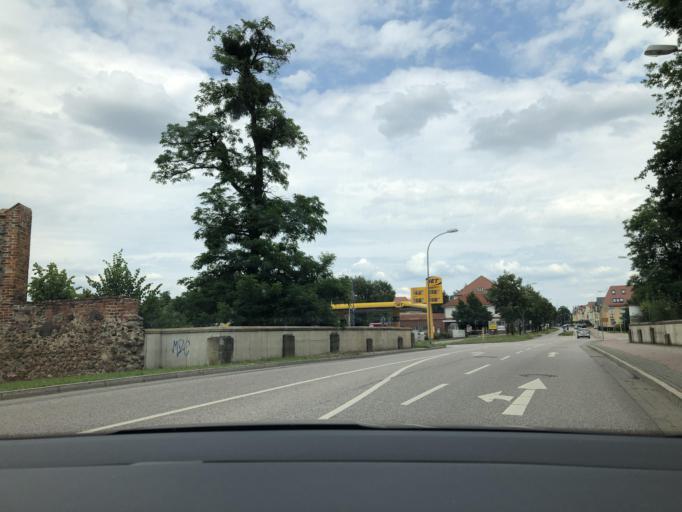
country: DE
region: Saxony-Anhalt
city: Zerbst
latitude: 51.9714
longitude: 12.0901
